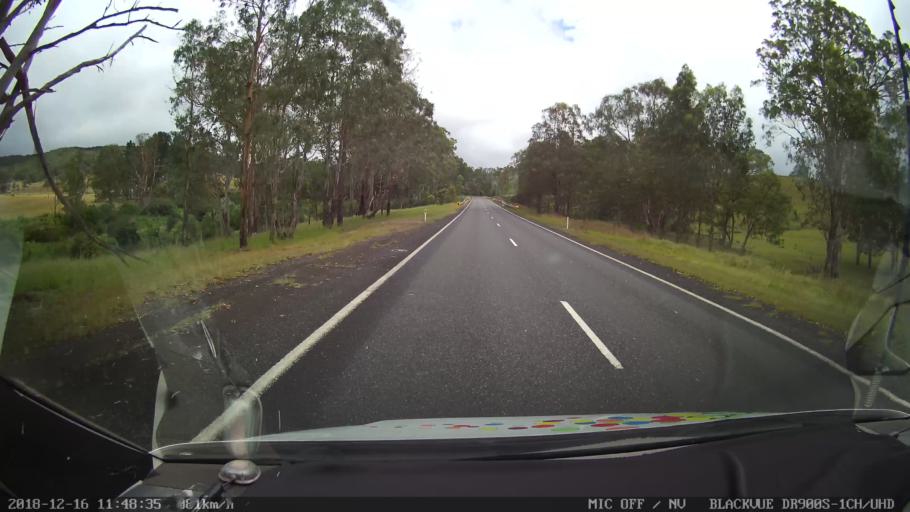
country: AU
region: New South Wales
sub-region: Tenterfield Municipality
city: Carrolls Creek
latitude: -28.9216
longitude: 152.2485
